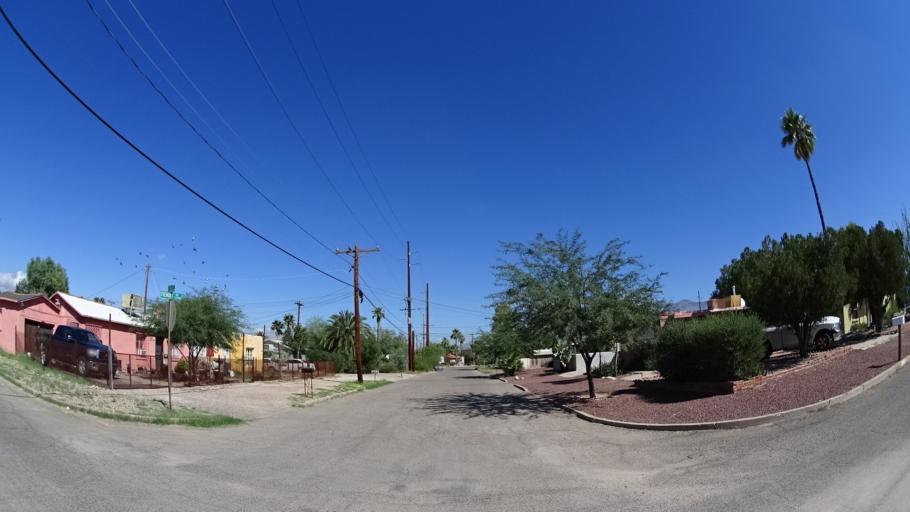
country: US
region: Arizona
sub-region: Pima County
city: Tucson
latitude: 32.2529
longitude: -110.9554
